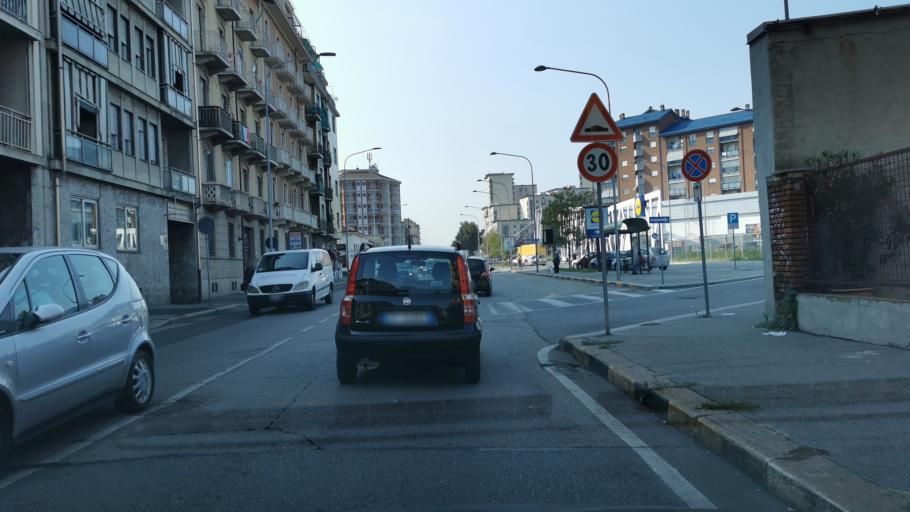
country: IT
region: Piedmont
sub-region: Provincia di Torino
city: Turin
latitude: 45.0963
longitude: 7.6885
